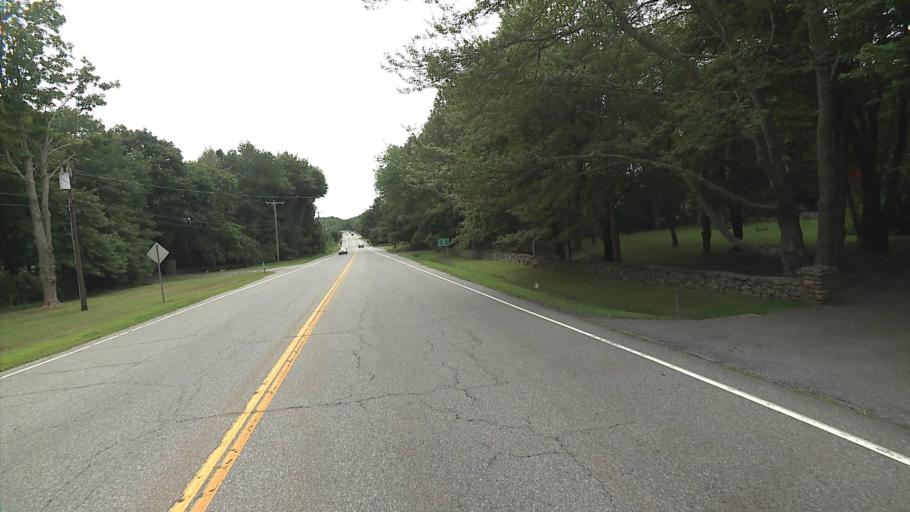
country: US
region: Connecticut
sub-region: Middlesex County
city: Old Saybrook Center
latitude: 41.3183
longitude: -72.3384
